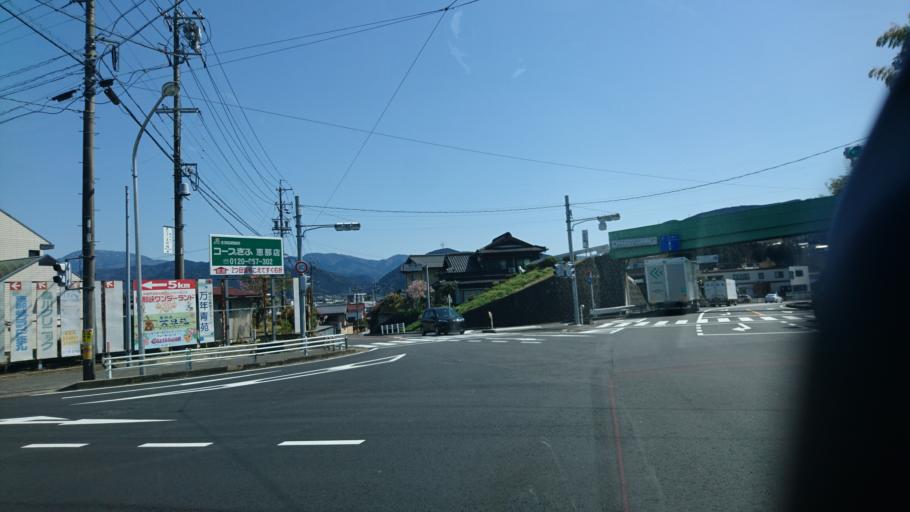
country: JP
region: Gifu
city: Nakatsugawa
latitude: 35.4520
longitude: 137.4008
